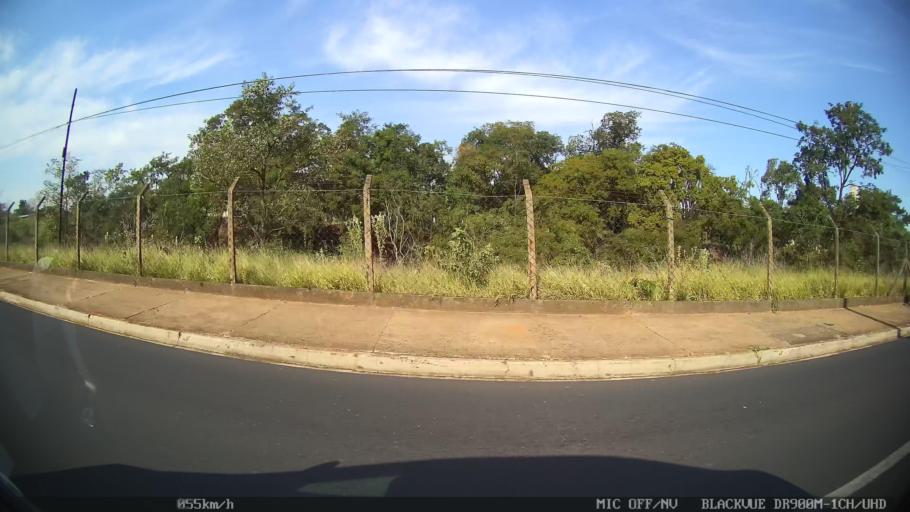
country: BR
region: Sao Paulo
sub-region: Araraquara
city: Araraquara
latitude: -21.7710
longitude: -48.1651
